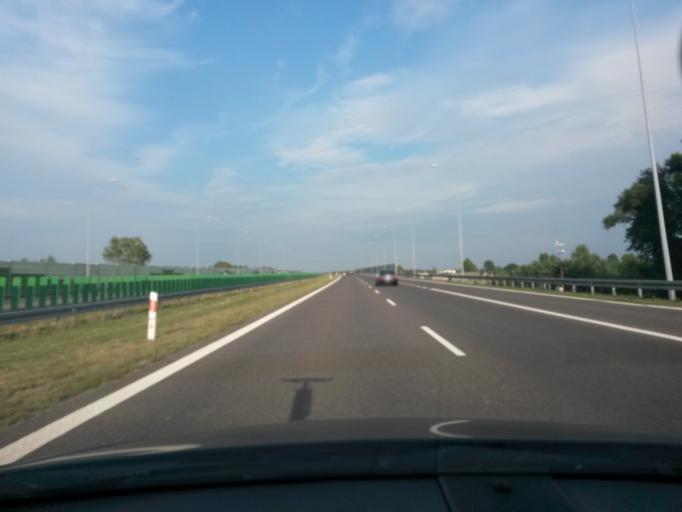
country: PL
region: Lodz Voivodeship
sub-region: Powiat zgierski
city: Ozorkow
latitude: 51.9218
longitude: 19.3551
